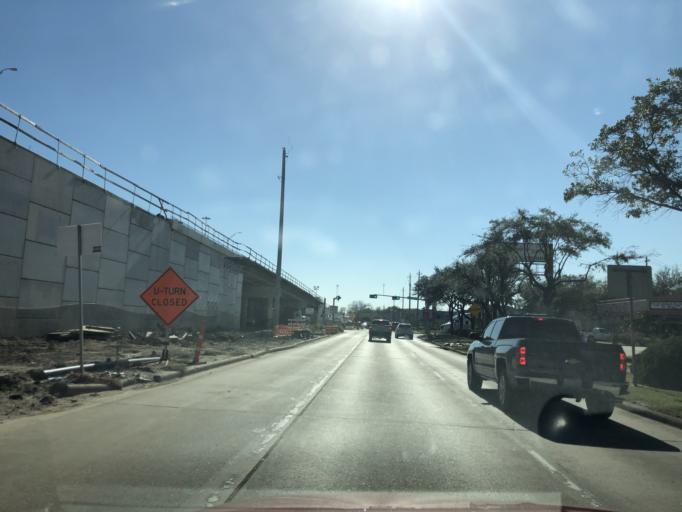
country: US
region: Texas
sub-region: Harris County
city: Deer Park
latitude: 29.6822
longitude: -95.1558
